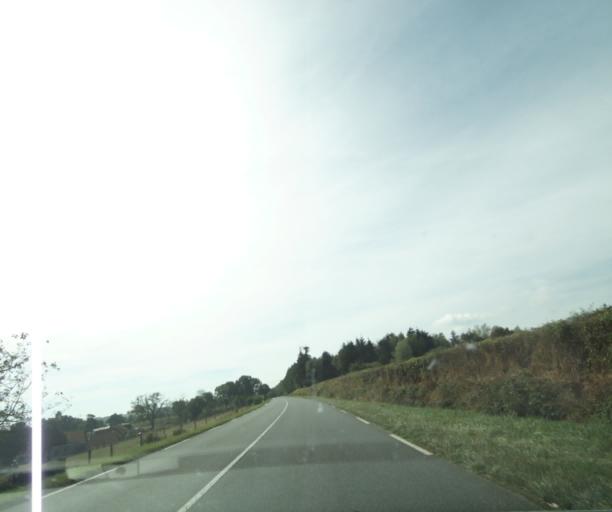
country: FR
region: Auvergne
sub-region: Departement de l'Allier
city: Le Donjon
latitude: 46.3263
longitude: 3.7665
